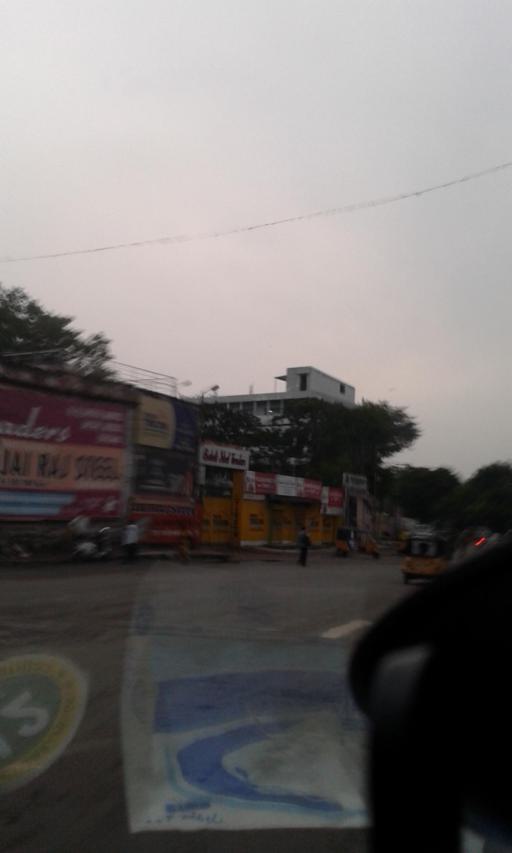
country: IN
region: Telangana
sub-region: Rangareddi
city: Gaddi Annaram
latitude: 17.3809
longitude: 78.4917
